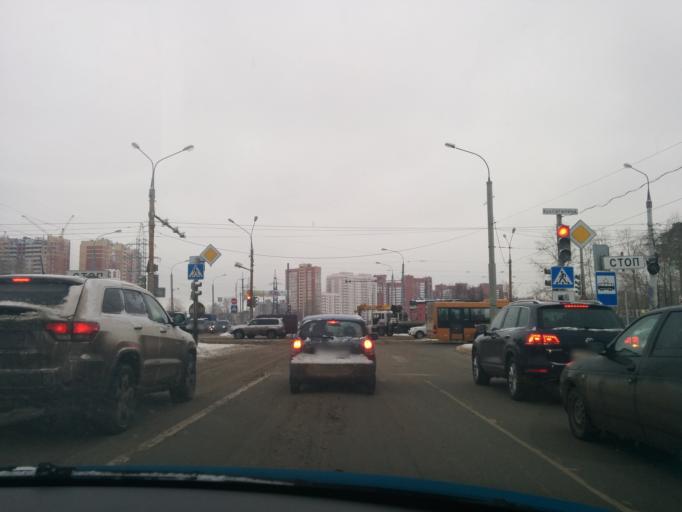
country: RU
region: Perm
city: Perm
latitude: 57.9906
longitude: 56.2977
